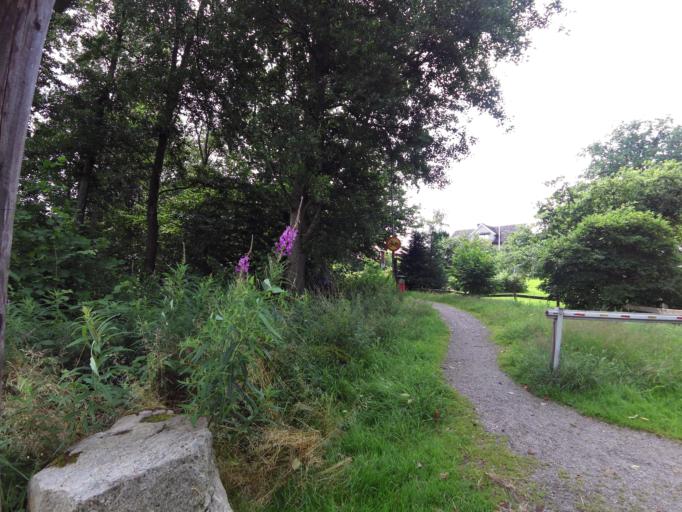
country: SE
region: Blekinge
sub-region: Olofstroms Kommun
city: Olofstroem
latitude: 56.3523
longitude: 14.5918
